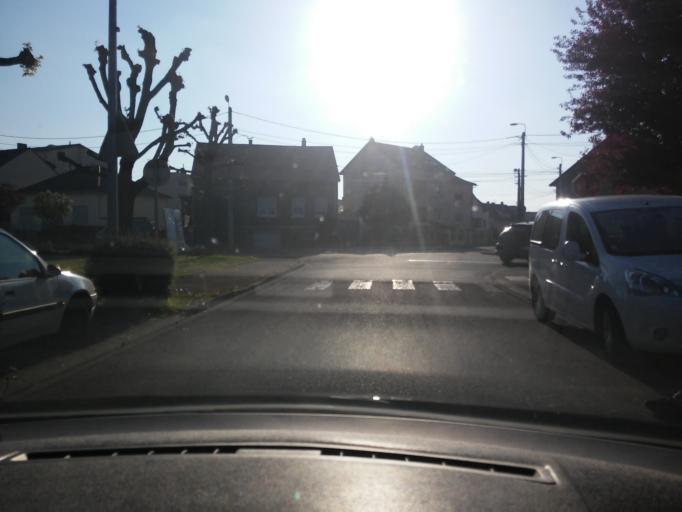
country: FR
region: Lorraine
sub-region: Departement de la Moselle
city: Talange
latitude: 49.2328
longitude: 6.1716
